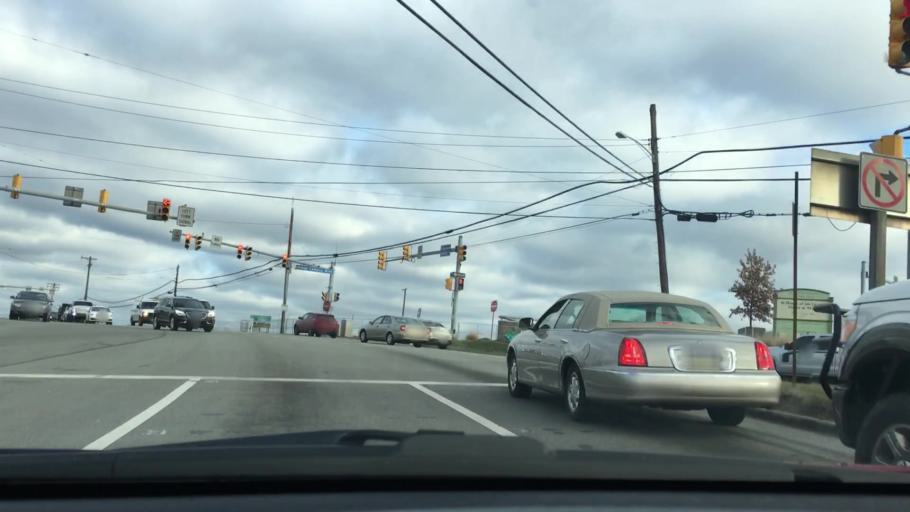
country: US
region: Pennsylvania
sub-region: Allegheny County
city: Pitcairn
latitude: 40.4294
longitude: -79.7514
